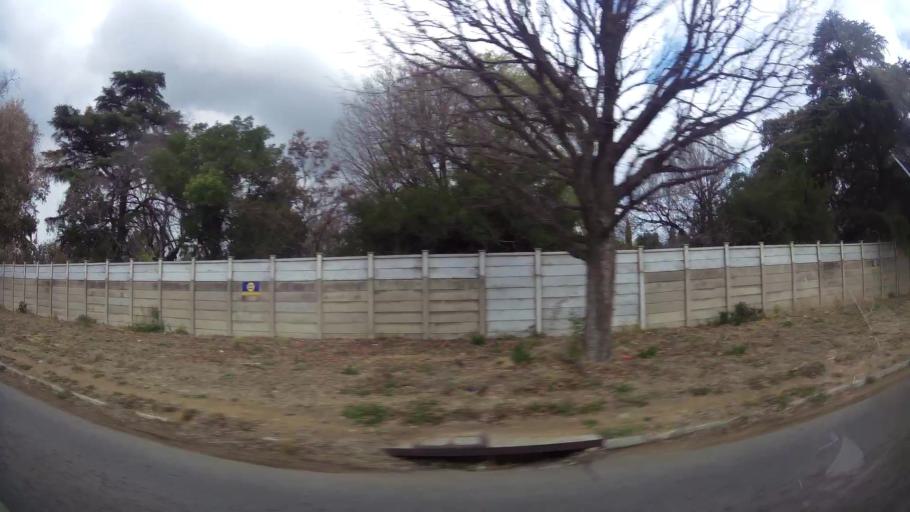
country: ZA
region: Orange Free State
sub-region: Fezile Dabi District Municipality
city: Sasolburg
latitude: -26.8043
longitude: 27.8315
